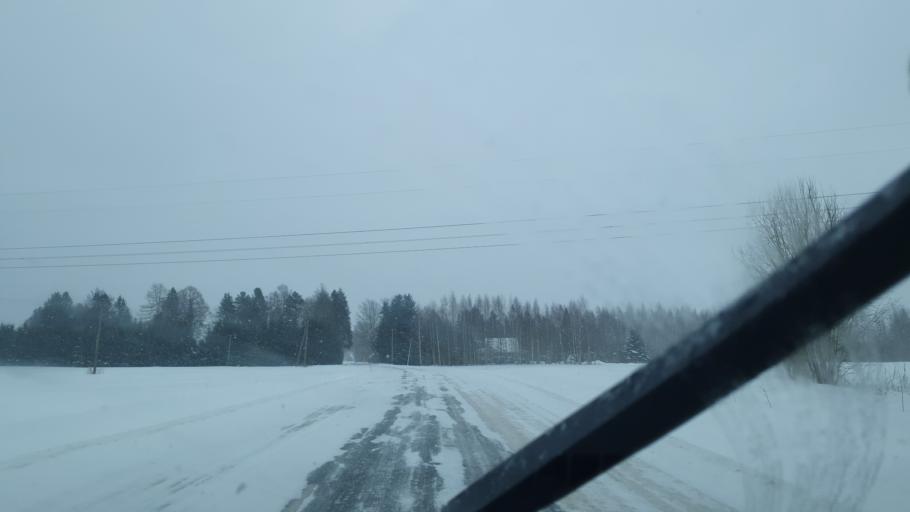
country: EE
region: Jogevamaa
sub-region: Tabivere vald
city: Tabivere
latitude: 58.5751
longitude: 26.7649
